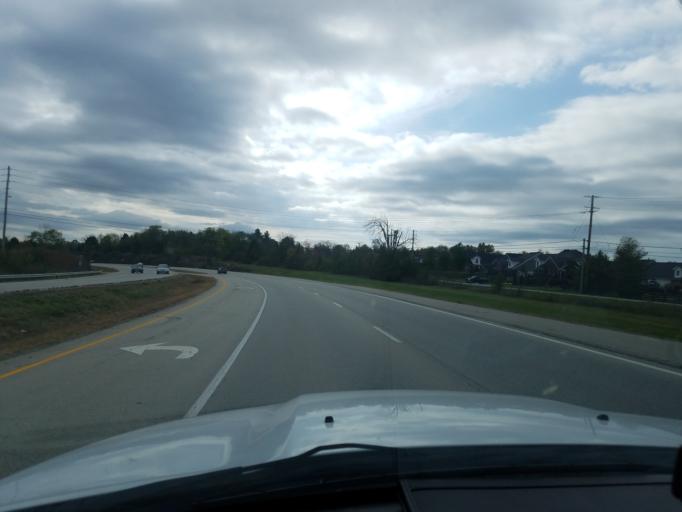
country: US
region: Kentucky
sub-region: Bullitt County
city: Mount Washington
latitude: 38.0993
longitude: -85.5656
